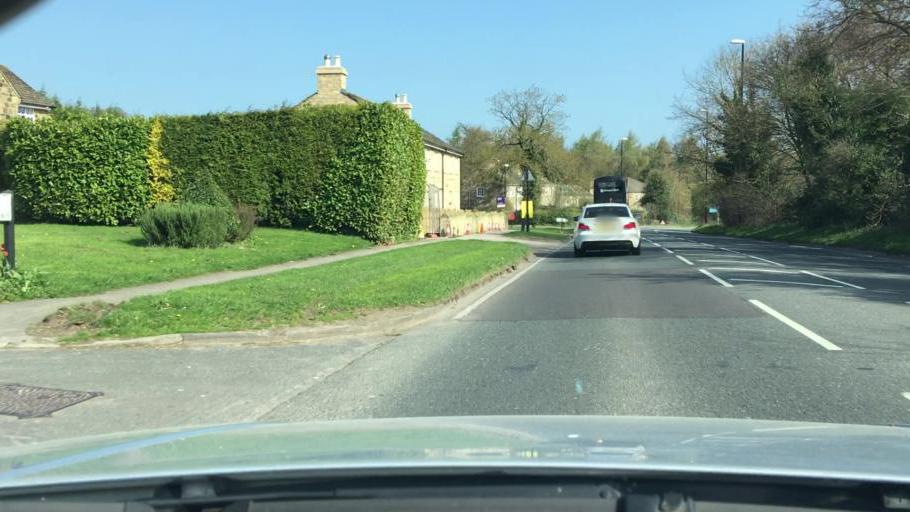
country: GB
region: England
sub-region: City and Borough of Leeds
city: East Keswick
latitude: 53.9027
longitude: -1.5119
